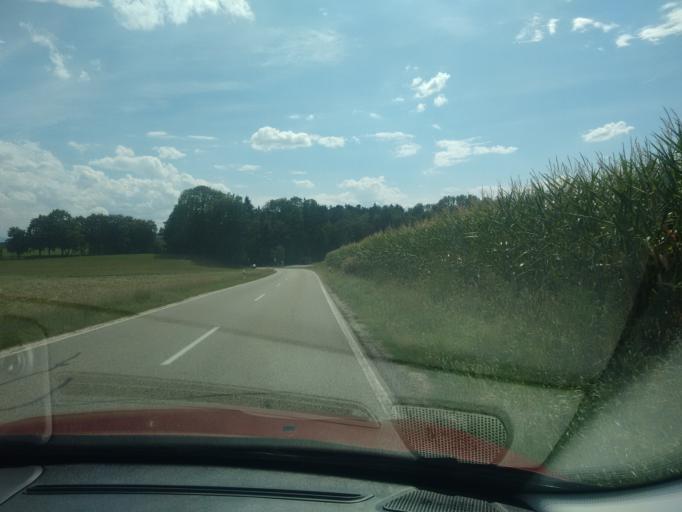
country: DE
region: Bavaria
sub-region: Upper Bavaria
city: Tacherting
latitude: 48.0552
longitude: 12.5929
